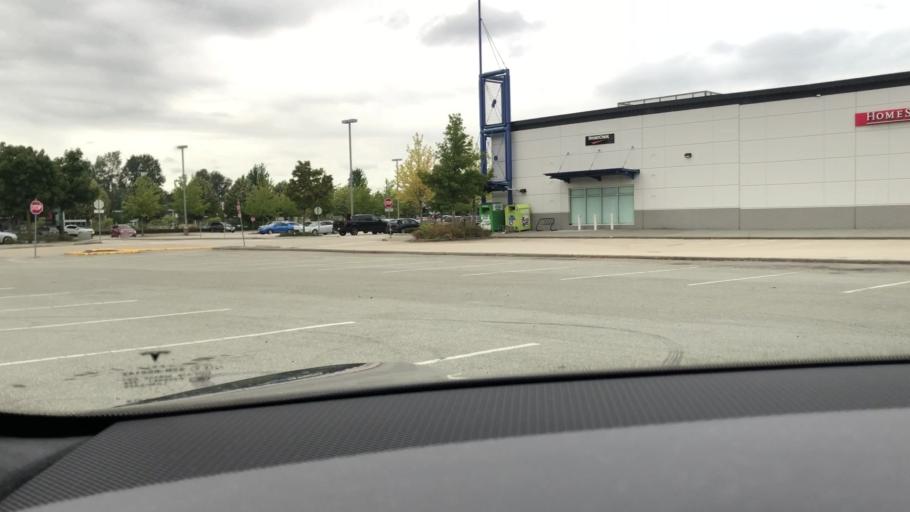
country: CA
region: British Columbia
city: New Westminster
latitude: 49.1985
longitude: -122.9743
